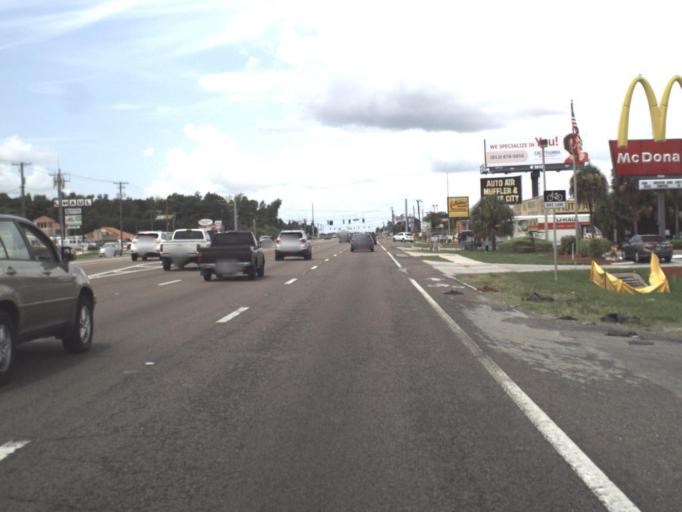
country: US
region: Florida
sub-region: Hillsborough County
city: Egypt Lake-Leto
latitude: 27.9963
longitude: -82.5165
